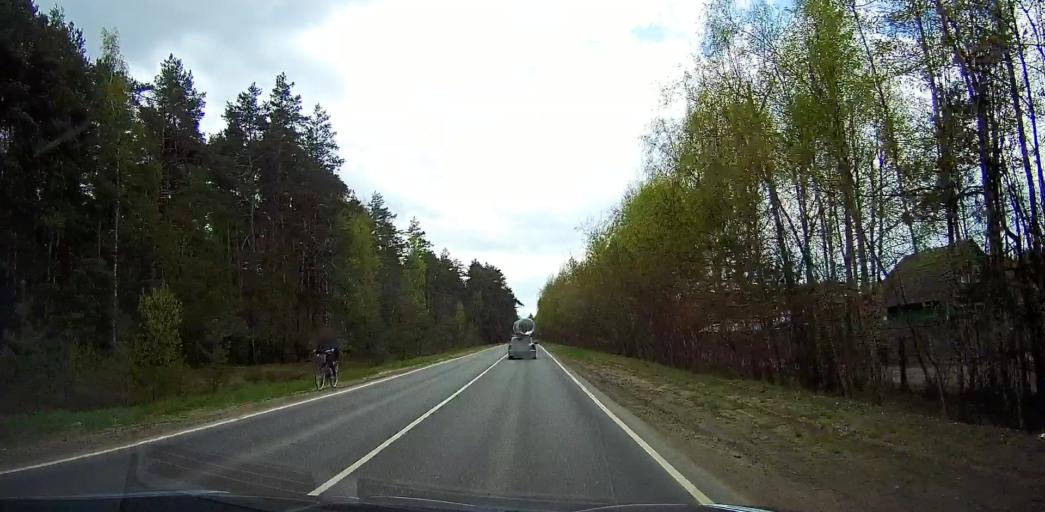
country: RU
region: Moskovskaya
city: Beloozerskiy
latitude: 55.4953
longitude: 38.4293
